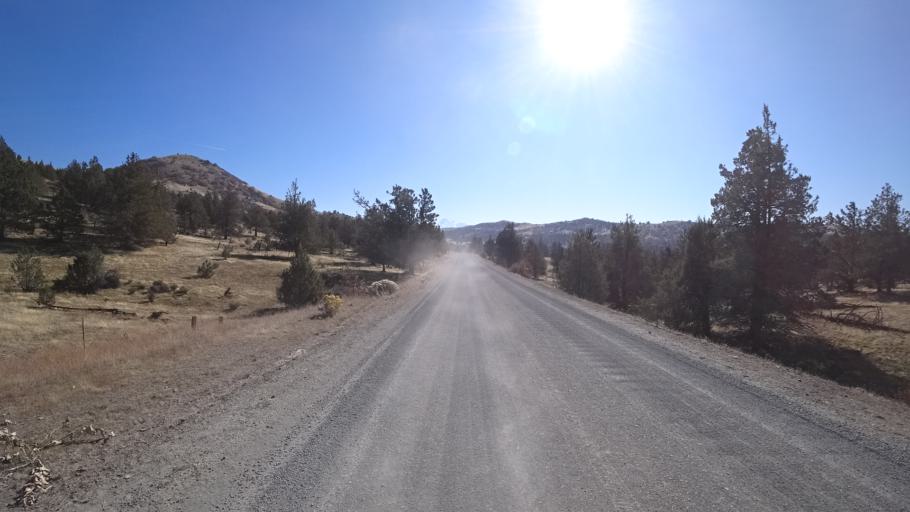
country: US
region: California
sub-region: Siskiyou County
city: Montague
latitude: 41.8050
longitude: -122.3710
